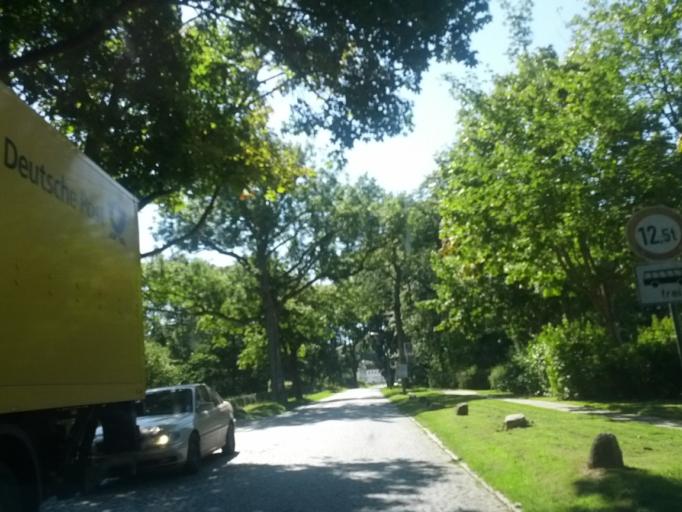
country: DE
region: Mecklenburg-Vorpommern
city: Bergen auf Ruegen
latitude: 54.4245
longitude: 13.4330
